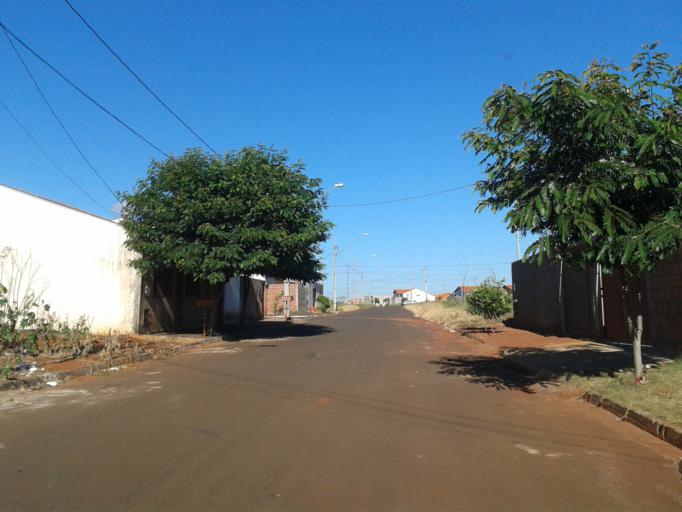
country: BR
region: Minas Gerais
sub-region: Santa Vitoria
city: Santa Vitoria
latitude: -18.8601
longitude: -50.1266
